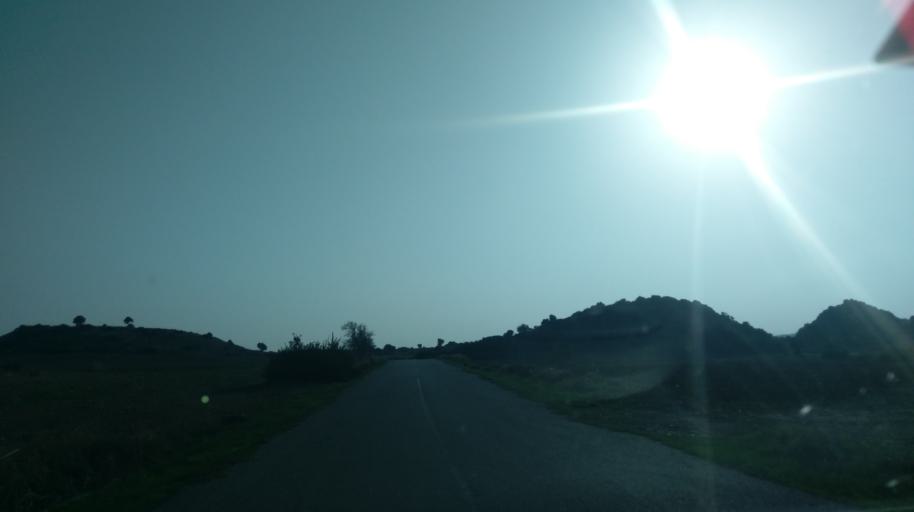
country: CY
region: Ammochostos
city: Leonarisso
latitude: 35.4576
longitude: 34.0963
